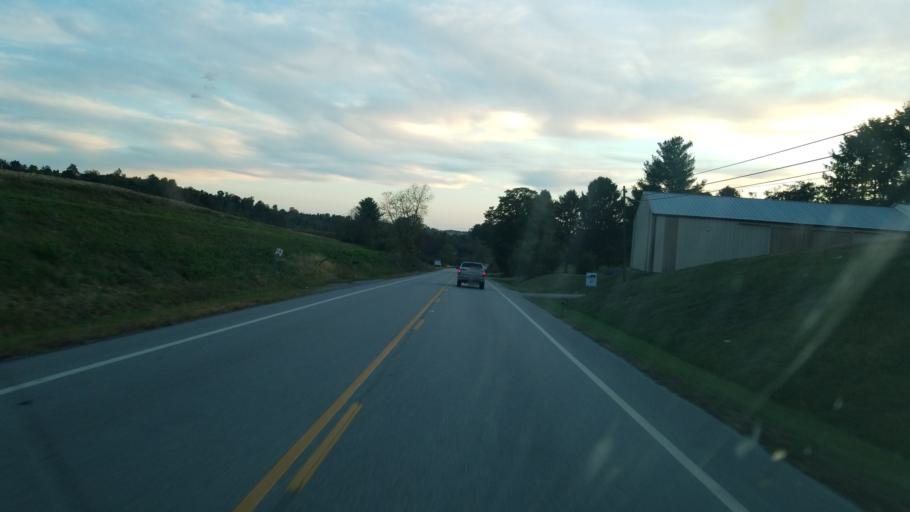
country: US
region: West Virginia
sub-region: Mason County
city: New Haven
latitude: 39.0763
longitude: -81.9307
